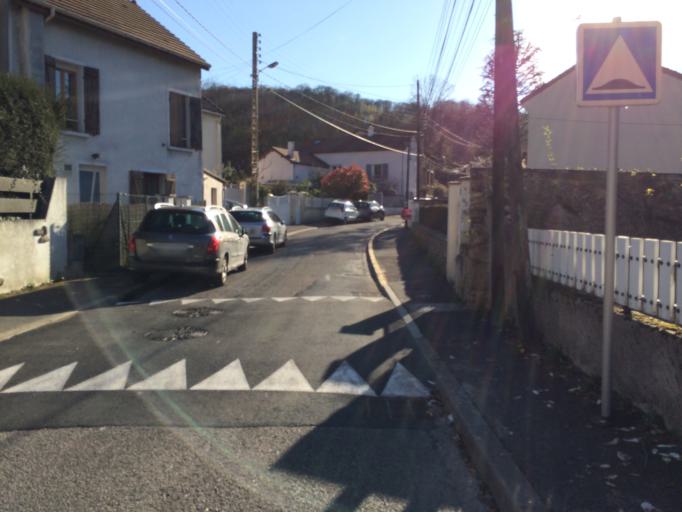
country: FR
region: Ile-de-France
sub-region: Departement de l'Essonne
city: Villebon-sur-Yvette
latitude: 48.6974
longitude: 2.2266
